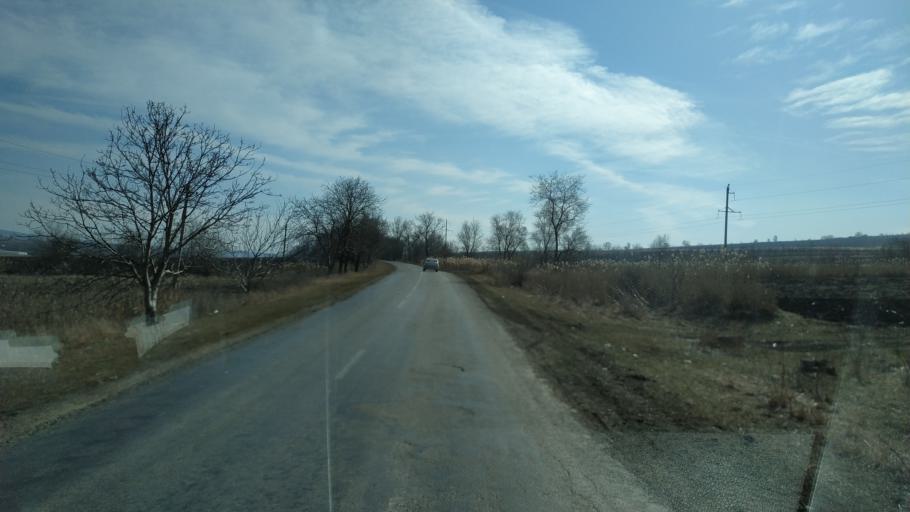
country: MD
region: Nisporeni
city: Nisporeni
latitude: 47.1042
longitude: 28.1264
